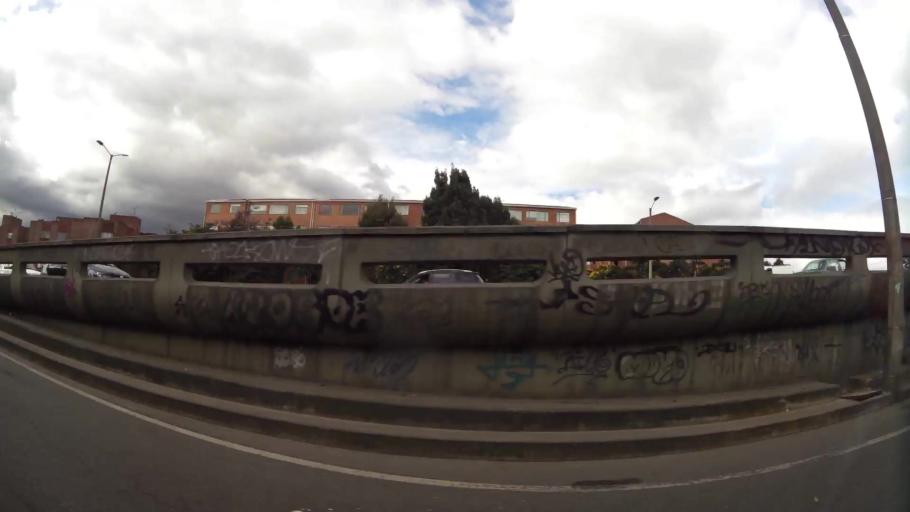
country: CO
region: Bogota D.C.
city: Bogota
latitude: 4.6099
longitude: -74.1301
